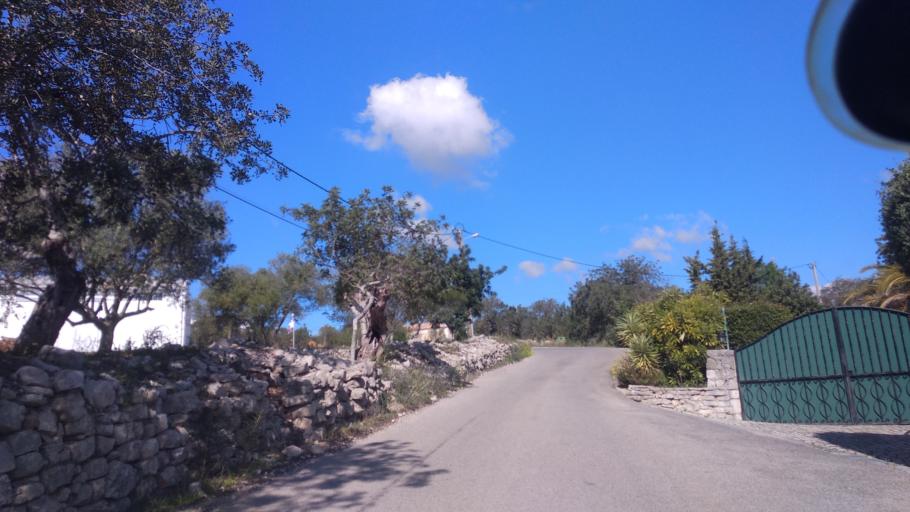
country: PT
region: Faro
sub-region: Sao Bras de Alportel
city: Sao Bras de Alportel
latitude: 37.1368
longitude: -7.9081
